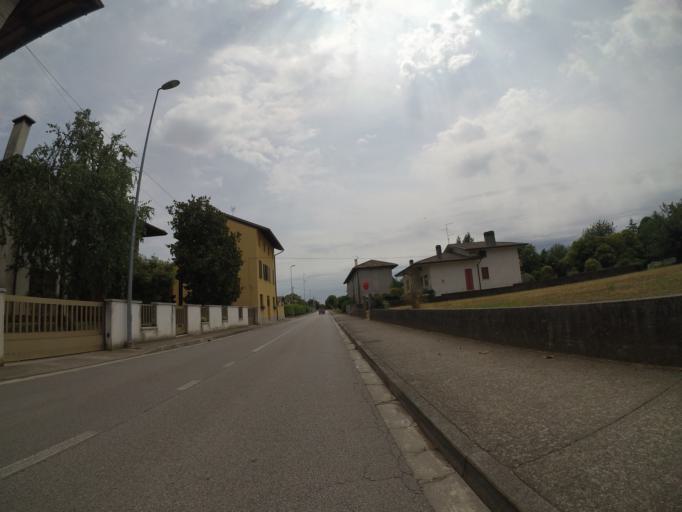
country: IT
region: Friuli Venezia Giulia
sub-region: Provincia di Udine
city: Sedegliano
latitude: 46.0119
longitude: 12.9771
